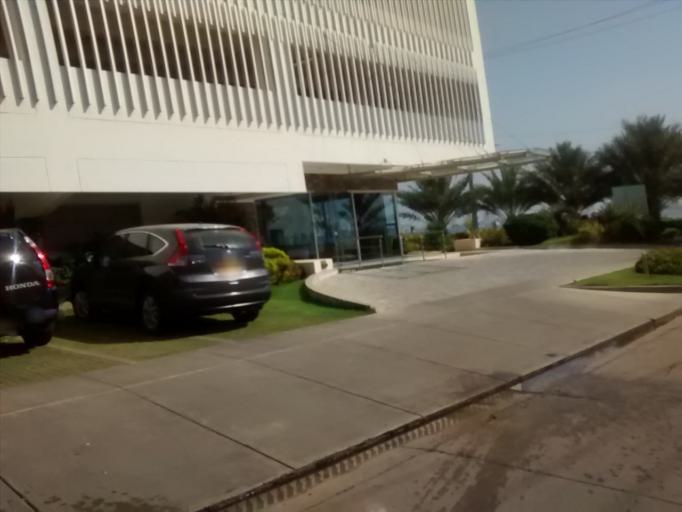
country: CO
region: Bolivar
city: Cartagena
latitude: 10.3924
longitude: -75.5468
